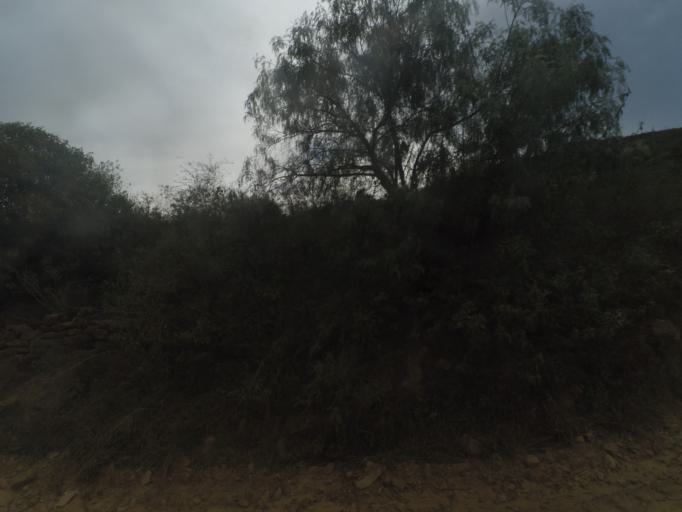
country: BO
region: Chuquisaca
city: Padilla
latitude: -19.3484
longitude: -64.2854
